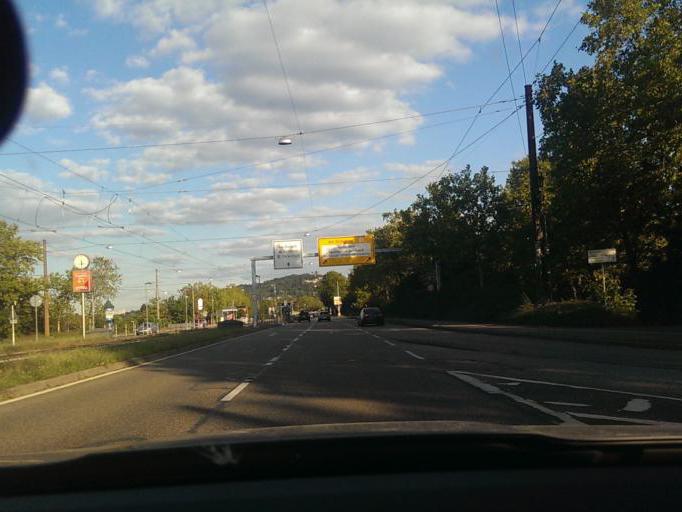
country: DE
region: Baden-Wuerttemberg
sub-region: Karlsruhe Region
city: Karlsruhe
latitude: 49.0023
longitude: 8.4527
